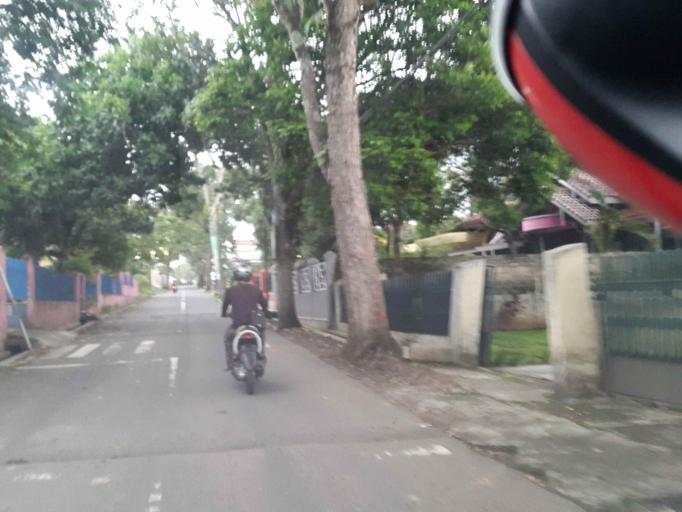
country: ID
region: West Java
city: Sukabumi
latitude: -6.9278
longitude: 106.9152
